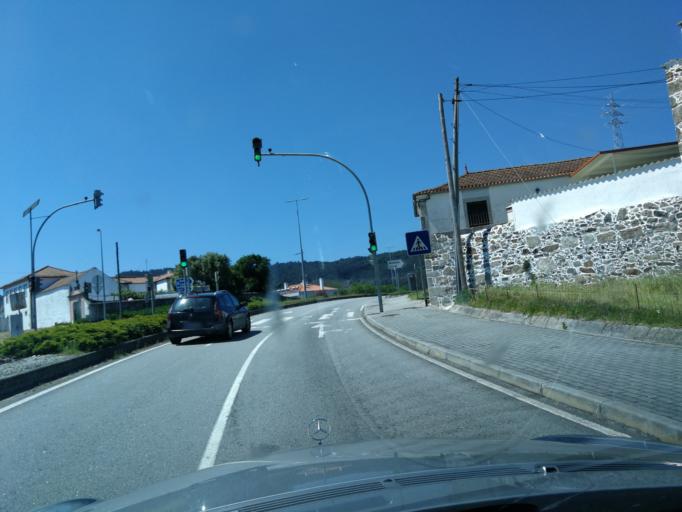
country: PT
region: Viana do Castelo
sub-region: Viana do Castelo
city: Meadela
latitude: 41.7095
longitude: -8.8067
